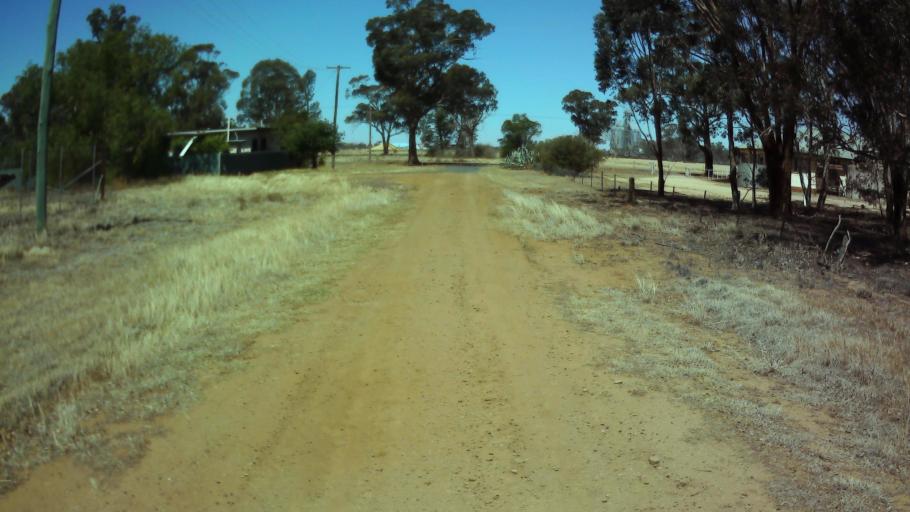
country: AU
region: New South Wales
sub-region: Weddin
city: Grenfell
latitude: -34.0143
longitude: 147.7928
